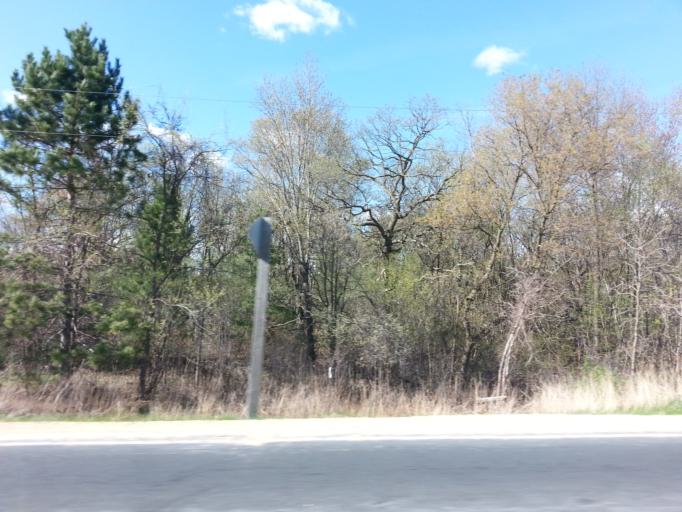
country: US
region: Minnesota
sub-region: Washington County
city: Bayport
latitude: 45.0573
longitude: -92.7357
